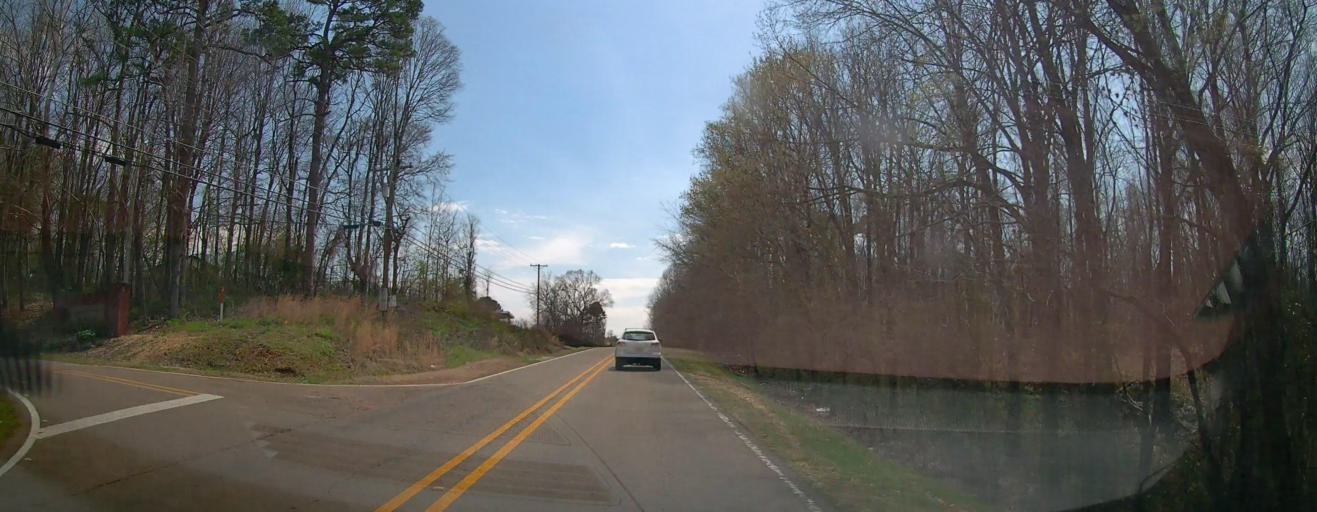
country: US
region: Mississippi
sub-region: Union County
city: New Albany
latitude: 34.4623
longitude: -88.9802
